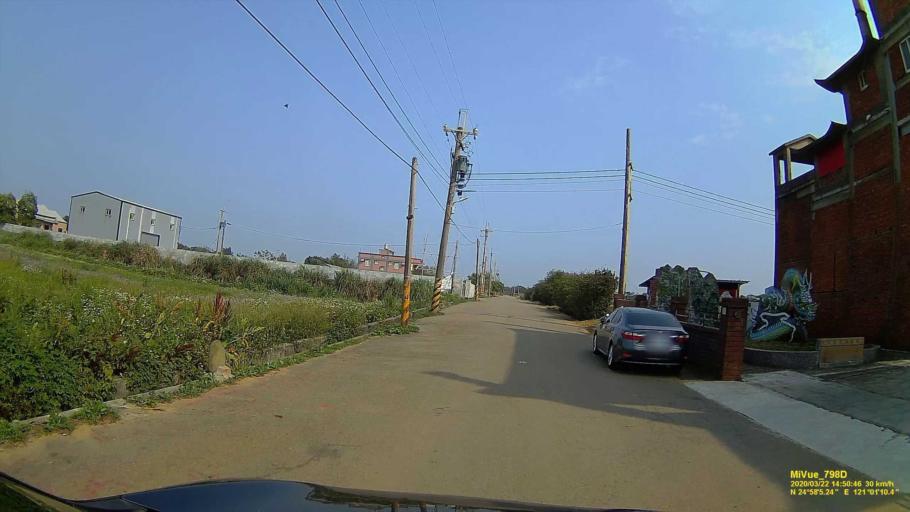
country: TW
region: Taiwan
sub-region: Hsinchu
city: Zhubei
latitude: 24.9681
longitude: 121.0198
